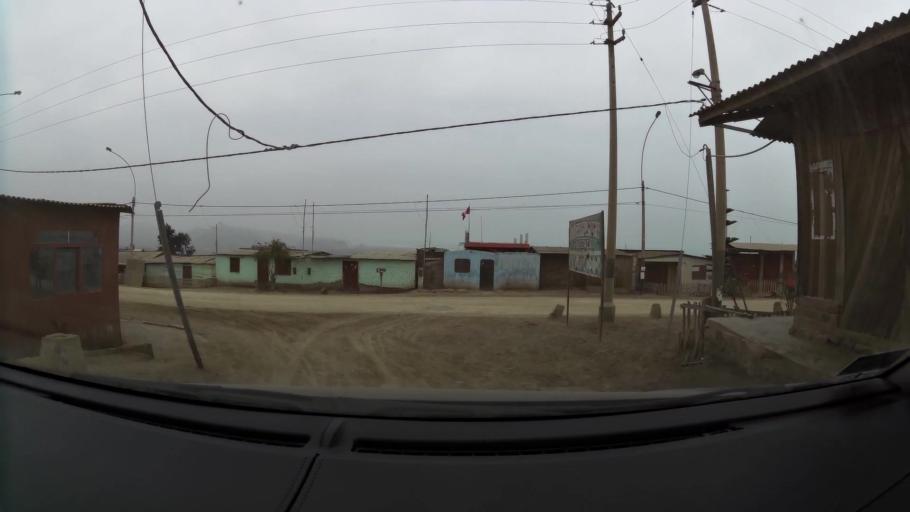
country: PE
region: Lima
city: Ventanilla
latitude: -11.8518
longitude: -77.1481
